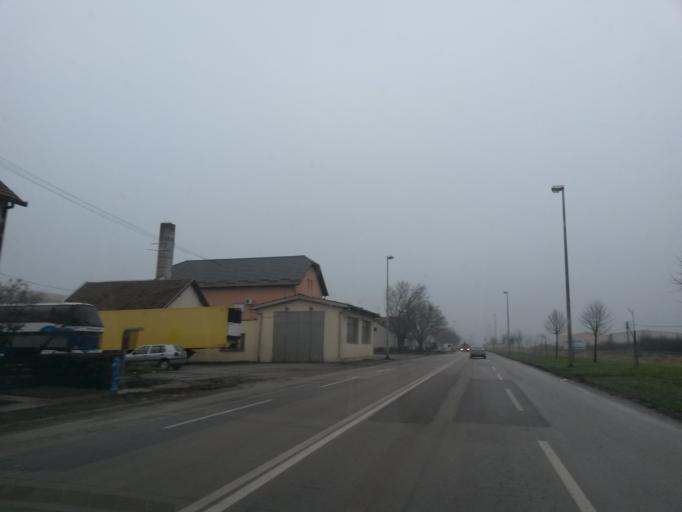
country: HR
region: Vukovarsko-Srijemska
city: Zupanja
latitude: 45.0920
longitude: 18.6971
